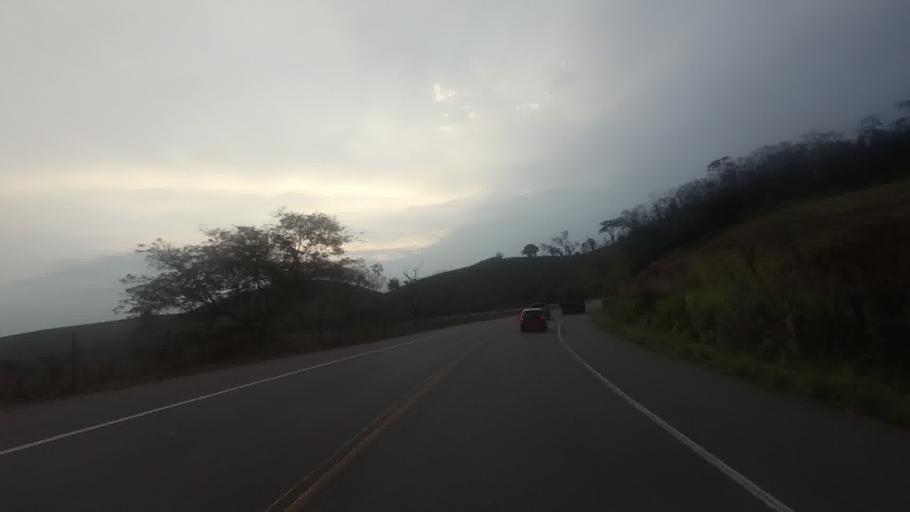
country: BR
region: Rio de Janeiro
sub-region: Carmo
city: Carmo
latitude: -21.8113
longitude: -42.5905
